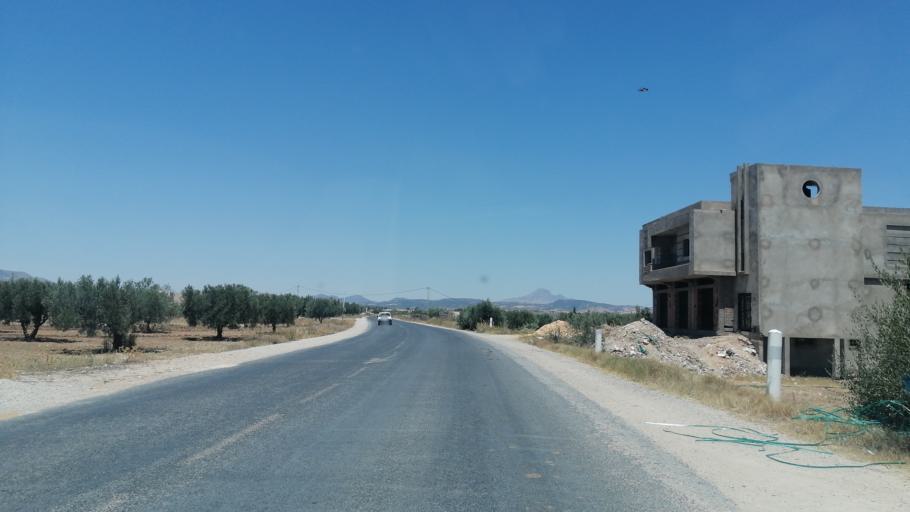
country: TN
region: Al Qayrawan
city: Sbikha
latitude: 36.1306
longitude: 10.0919
